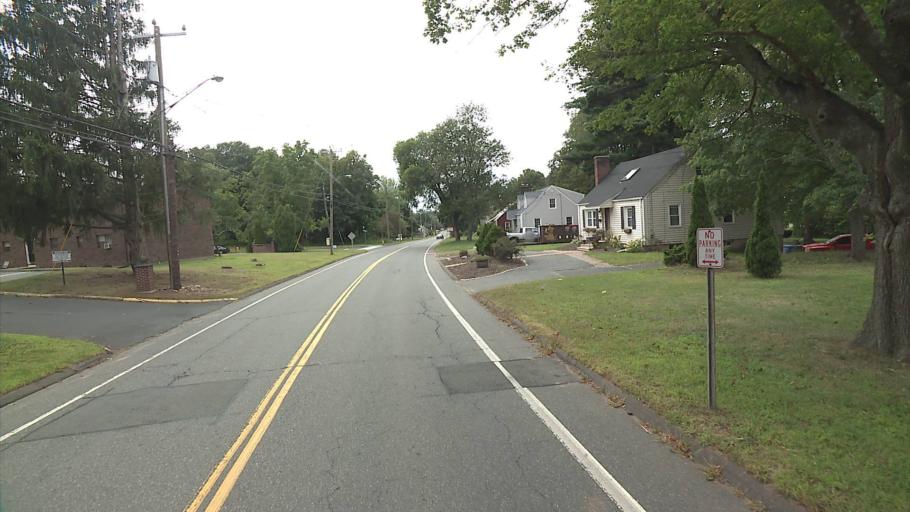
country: US
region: Connecticut
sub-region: Hartford County
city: Manchester
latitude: 41.7644
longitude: -72.5052
